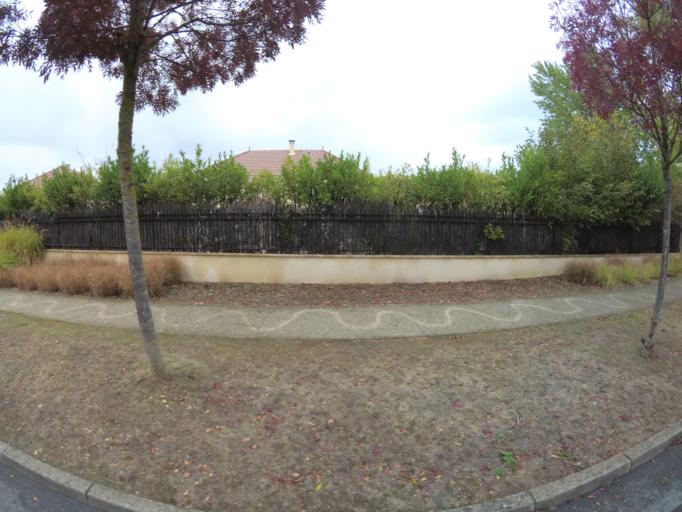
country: FR
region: Ile-de-France
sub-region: Departement de Seine-et-Marne
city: Montevrain
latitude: 48.8672
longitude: 2.7585
